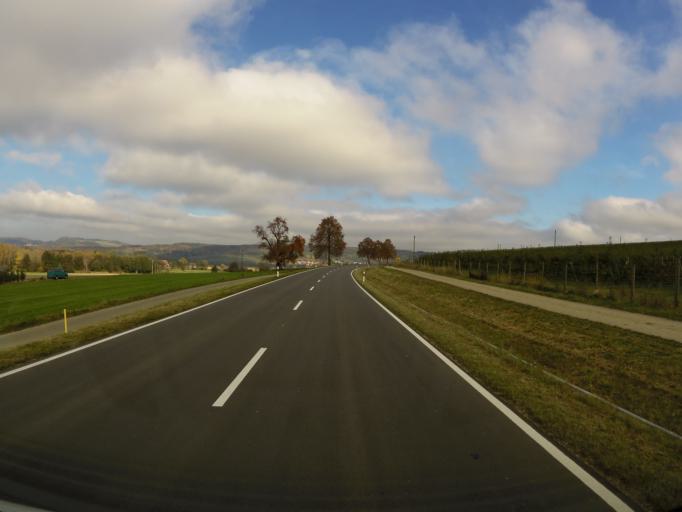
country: DE
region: Baden-Wuerttemberg
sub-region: Freiburg Region
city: Orsingen-Nenzingen
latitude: 47.7993
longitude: 8.9873
